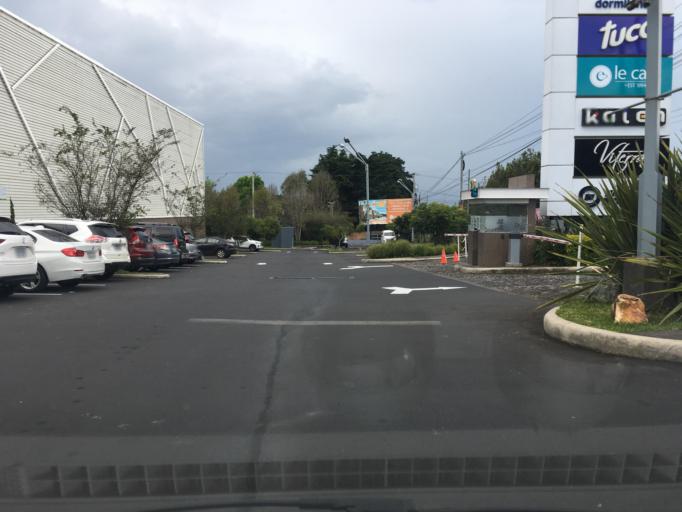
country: GT
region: Guatemala
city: Fraijanes
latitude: 14.4961
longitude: -90.4819
